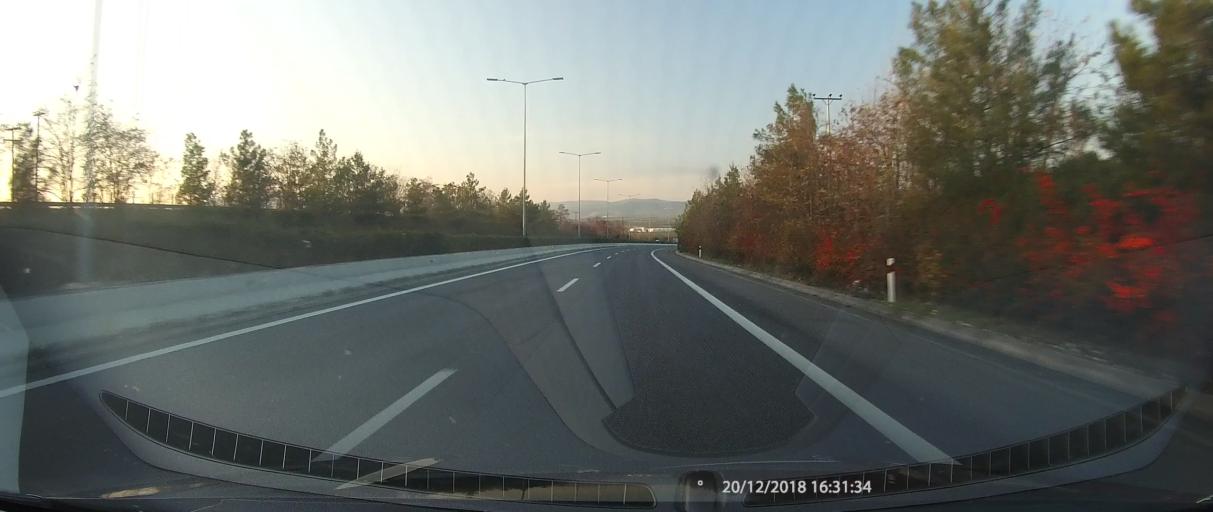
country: GR
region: Thessaly
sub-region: Nomos Magnisias
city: Evxinoupolis
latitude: 39.2287
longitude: 22.7400
